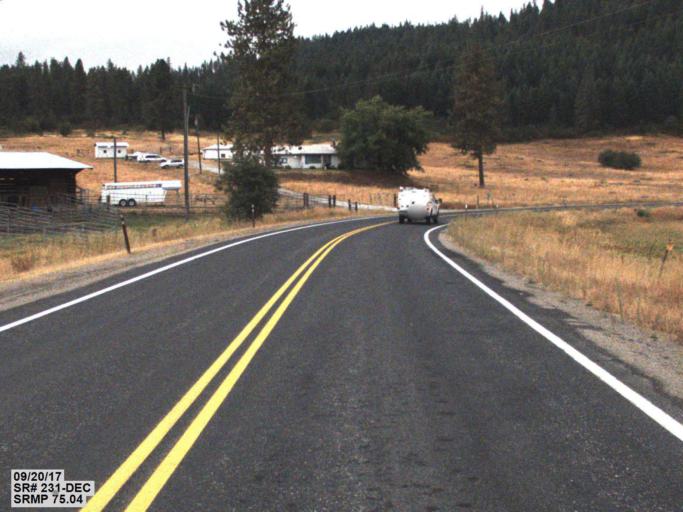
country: US
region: Washington
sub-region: Stevens County
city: Chewelah
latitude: 48.2070
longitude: -117.7169
